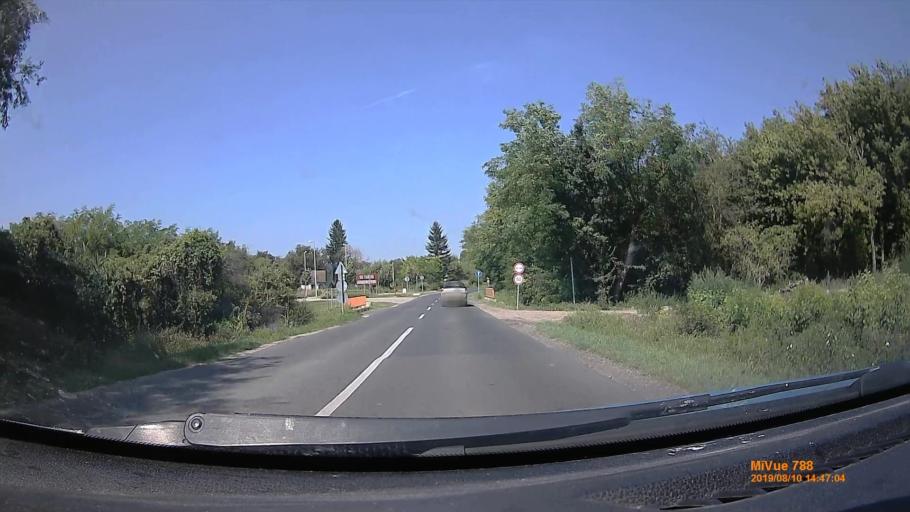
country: HU
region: Somogy
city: Somogyvar
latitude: 46.5959
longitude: 17.6435
